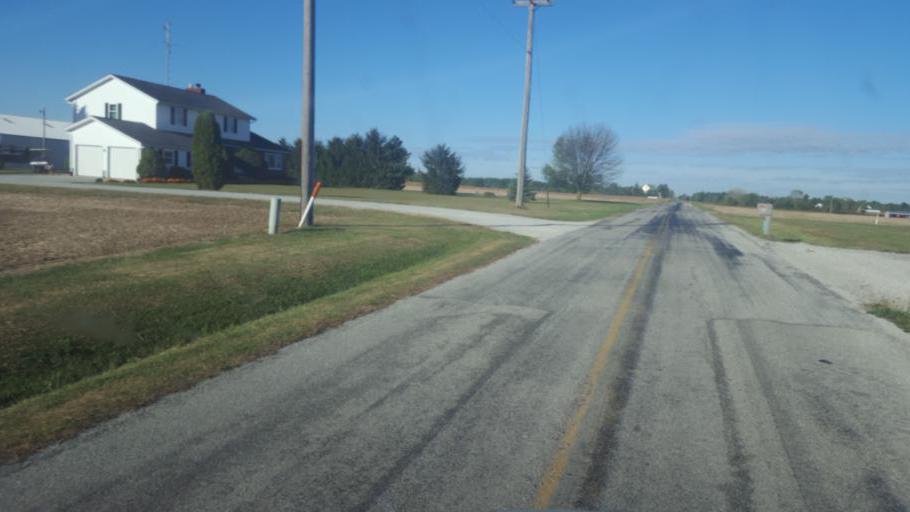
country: US
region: Ohio
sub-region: Crawford County
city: Galion
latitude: 40.6899
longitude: -82.9107
